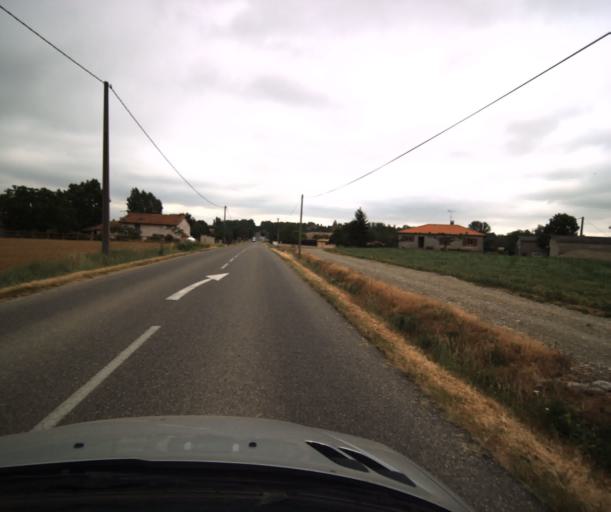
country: FR
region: Midi-Pyrenees
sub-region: Departement du Tarn-et-Garonne
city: Saint-Nicolas-de-la-Grave
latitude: 44.0319
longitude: 1.0322
